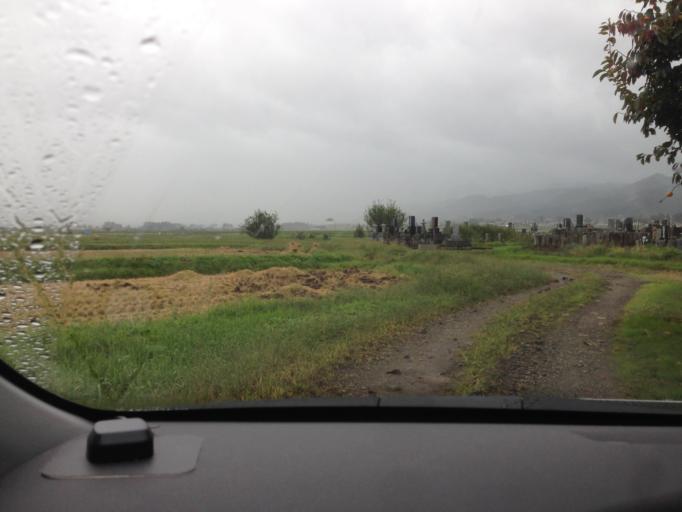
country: JP
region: Fukushima
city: Kitakata
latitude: 37.4752
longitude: 139.8293
